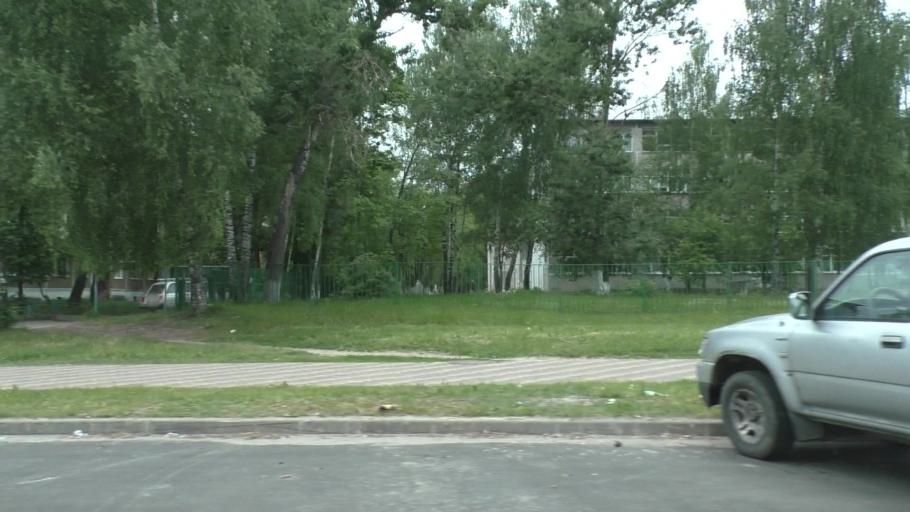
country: RU
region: Moskovskaya
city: Yegor'yevsk
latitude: 55.3661
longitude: 39.0638
